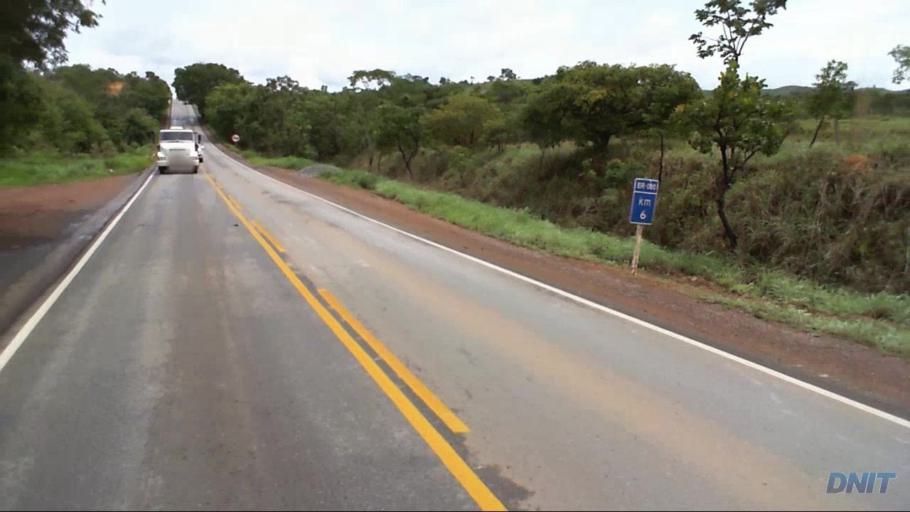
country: BR
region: Goias
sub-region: Padre Bernardo
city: Padre Bernardo
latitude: -15.4802
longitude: -48.2341
